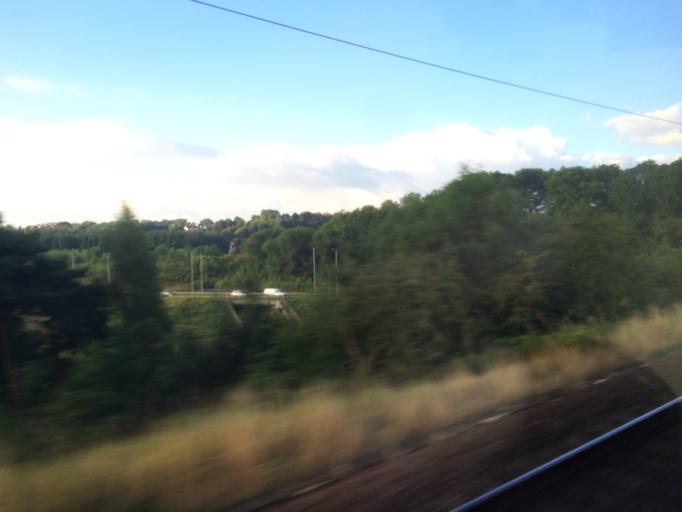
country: GB
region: Scotland
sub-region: East Dunbartonshire
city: Kirkintilloch
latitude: 55.9251
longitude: -4.1378
